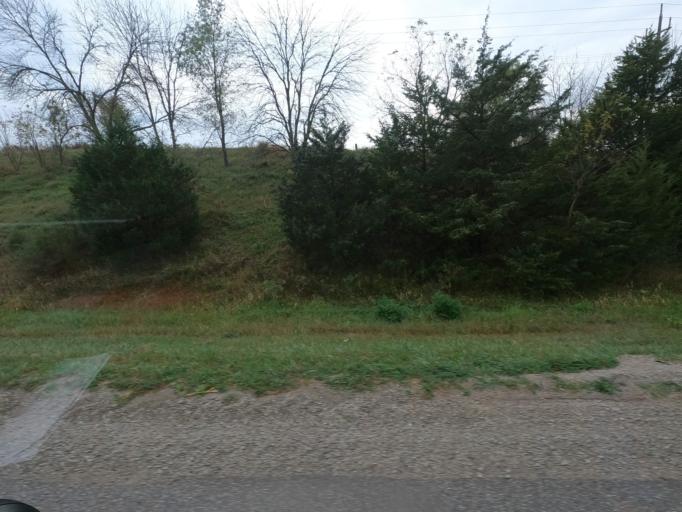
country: US
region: Iowa
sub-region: Van Buren County
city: Keosauqua
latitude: 40.8190
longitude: -91.9436
